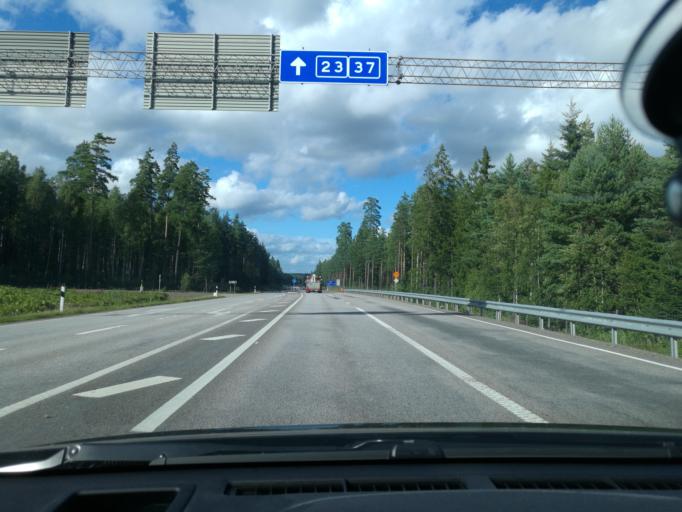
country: SE
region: Kronoberg
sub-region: Vaxjo Kommun
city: Braas
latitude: 57.0175
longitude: 15.0546
